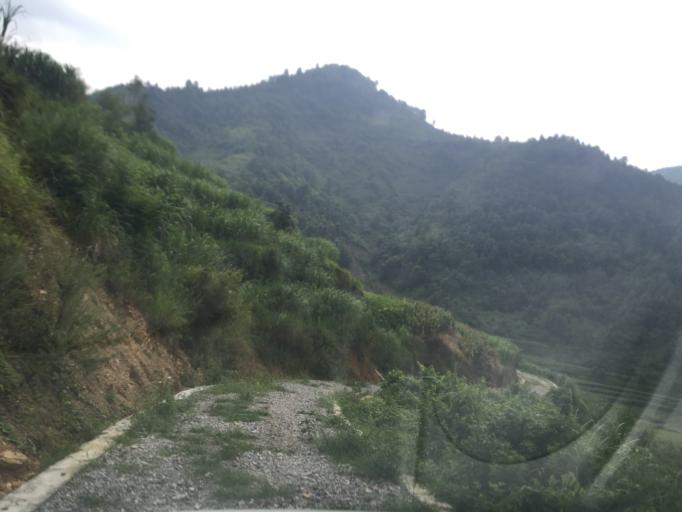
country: CN
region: Guangxi Zhuangzu Zizhiqu
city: Xinzhou
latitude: 25.1684
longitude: 105.6984
